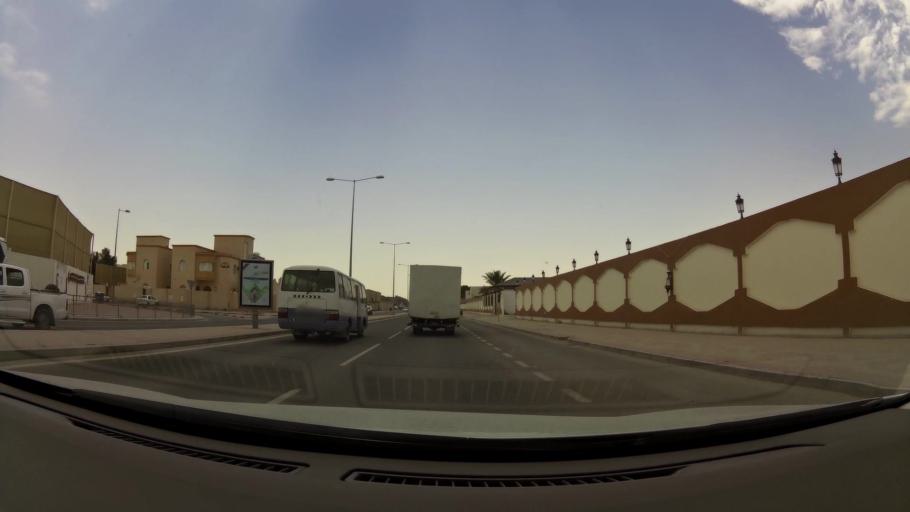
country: QA
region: Baladiyat ar Rayyan
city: Ar Rayyan
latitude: 25.2550
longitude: 51.4182
